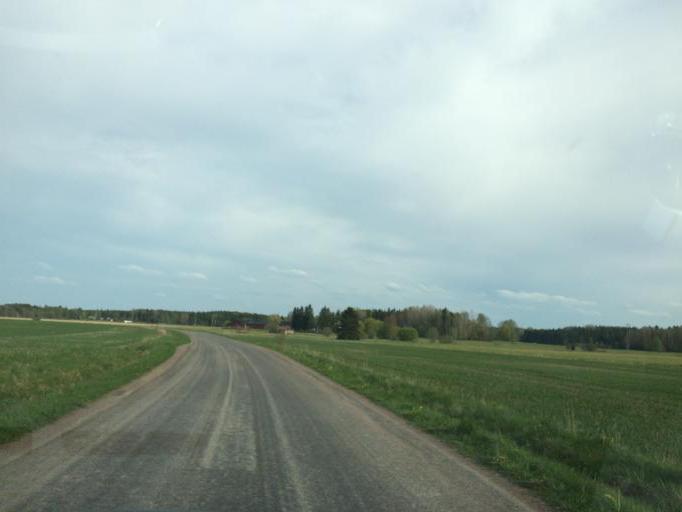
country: SE
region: Vaestmanland
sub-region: Hallstahammars Kommun
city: Hallstahammar
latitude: 59.5979
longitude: 16.1364
